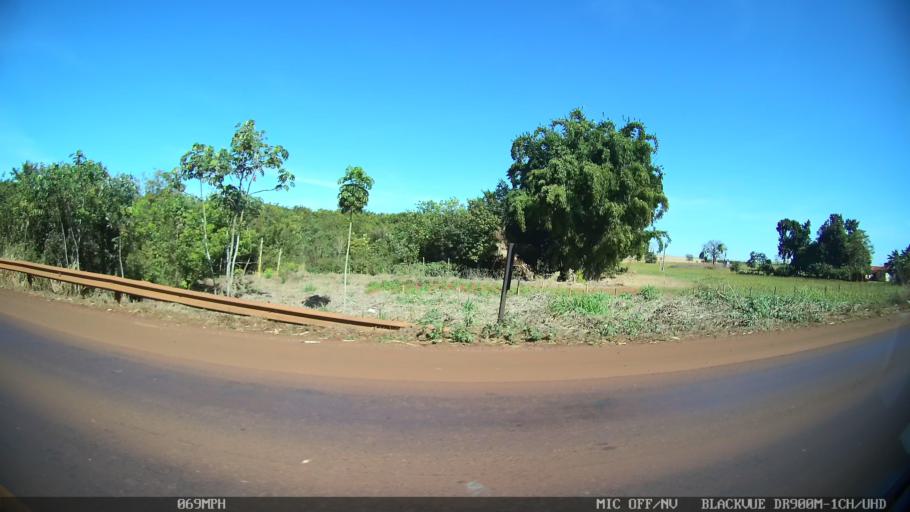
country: BR
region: Sao Paulo
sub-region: Ipua
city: Ipua
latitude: -20.4925
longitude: -47.9881
